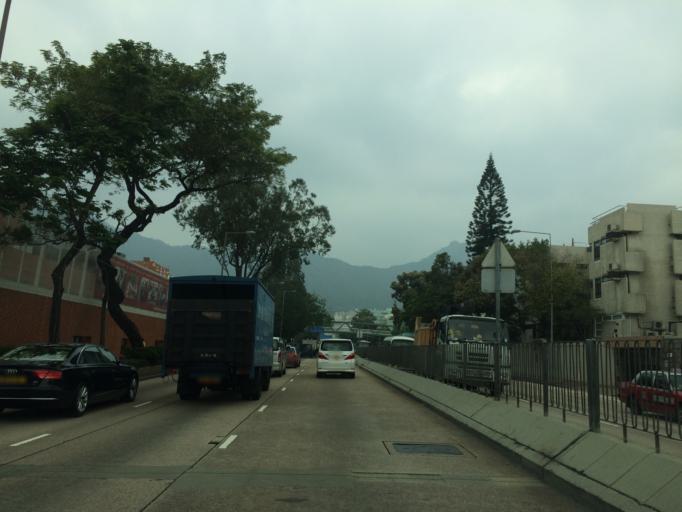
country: HK
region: Kowloon City
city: Kowloon
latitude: 22.3310
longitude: 114.1786
